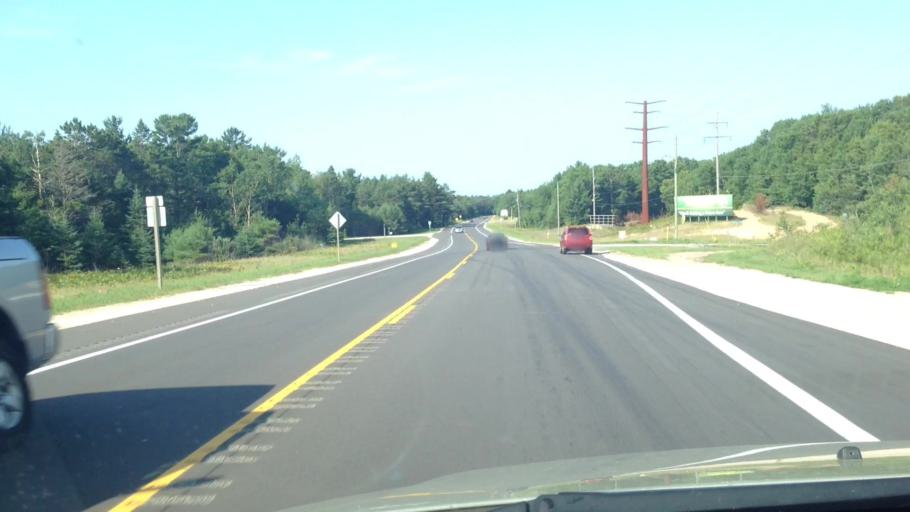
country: US
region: Michigan
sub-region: Schoolcraft County
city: Manistique
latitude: 45.9667
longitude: -86.2034
